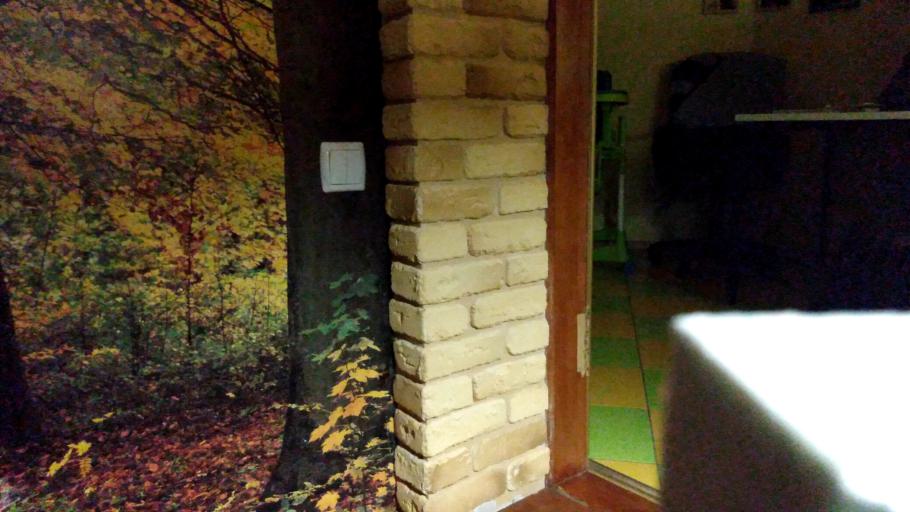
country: RU
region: Vologda
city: Lipin Bor
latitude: 61.0137
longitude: 37.9559
